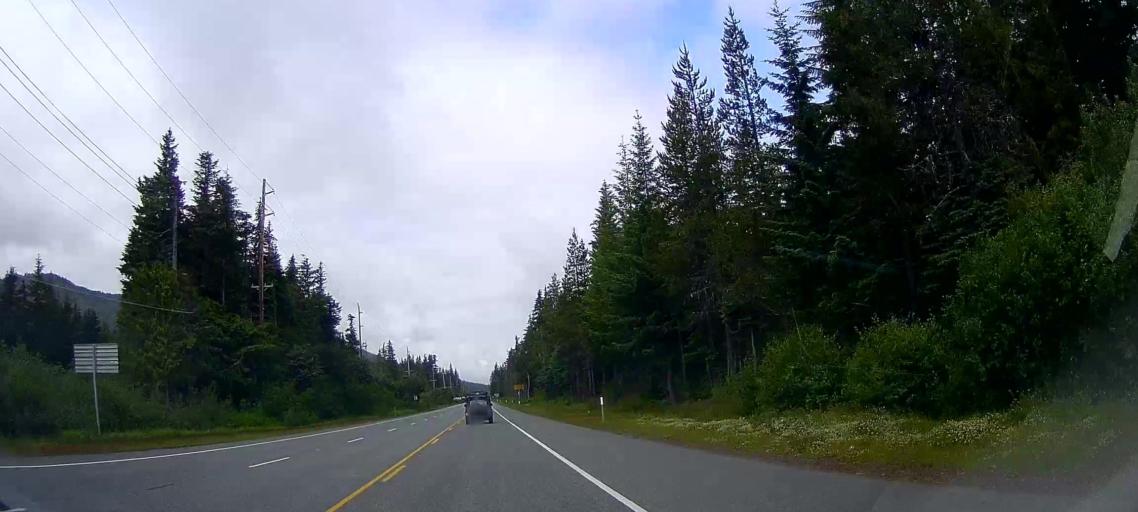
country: US
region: Oregon
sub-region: Clackamas County
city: Mount Hood Village
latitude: 45.3024
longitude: -121.7561
